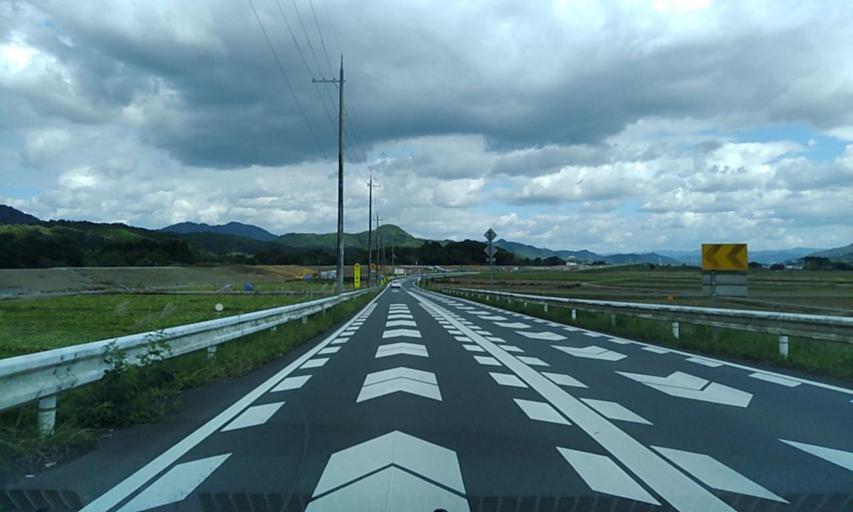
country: JP
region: Kyoto
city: Fukuchiyama
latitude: 35.3018
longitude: 135.1460
